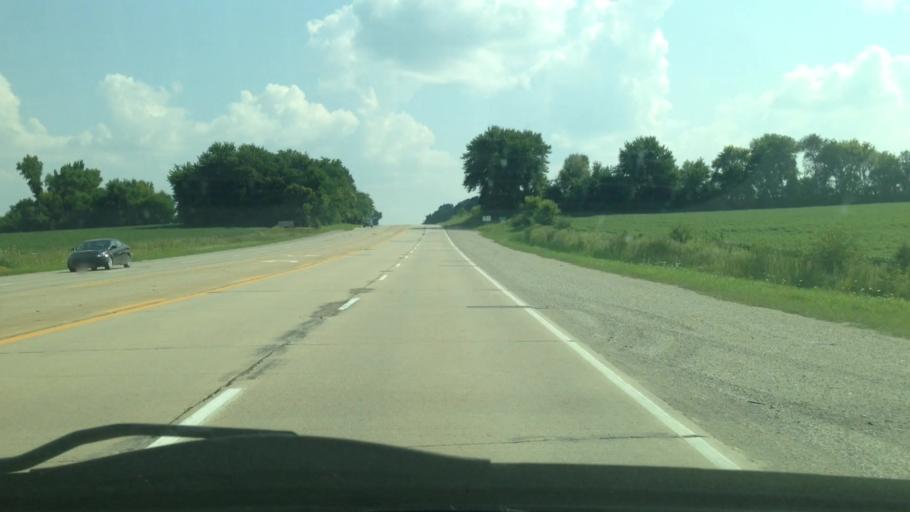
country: US
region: Iowa
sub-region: Black Hawk County
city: Waterloo
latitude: 42.5651
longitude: -92.3377
